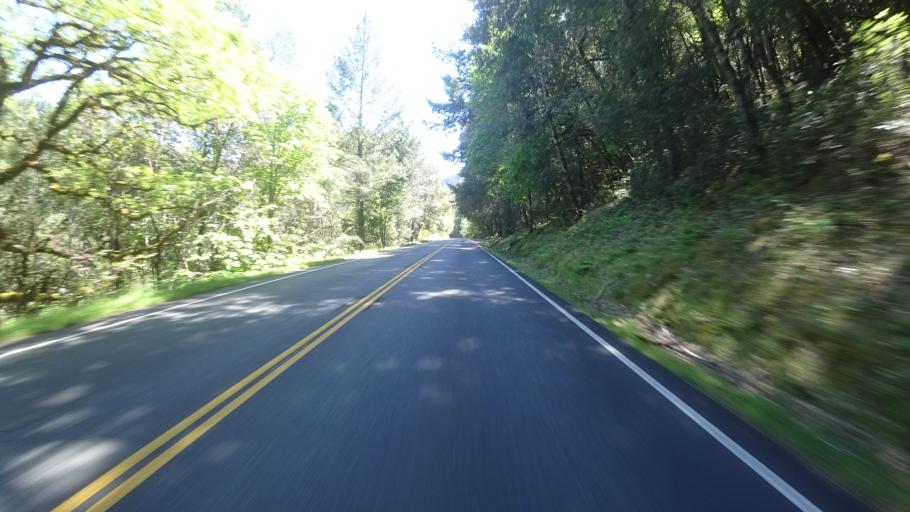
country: US
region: California
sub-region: Humboldt County
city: Willow Creek
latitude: 40.8661
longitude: -123.5190
